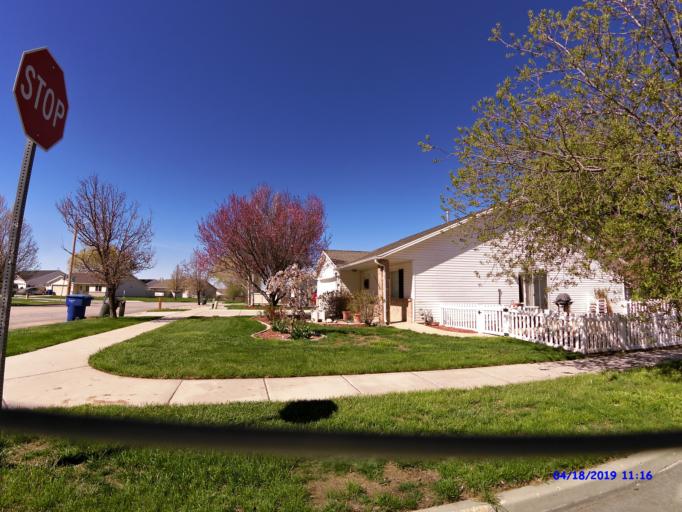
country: US
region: Utah
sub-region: Weber County
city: North Ogden
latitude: 41.2832
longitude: -111.9578
